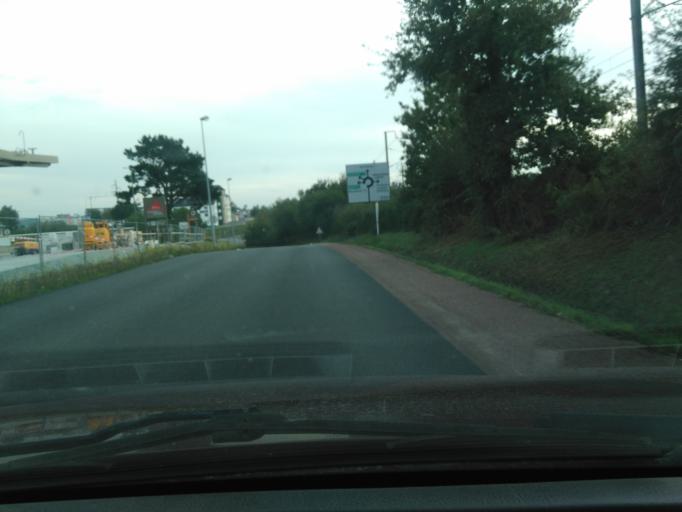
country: FR
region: Pays de la Loire
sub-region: Departement de la Vendee
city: Mouilleron-le-Captif
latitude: 46.7138
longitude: -1.4315
